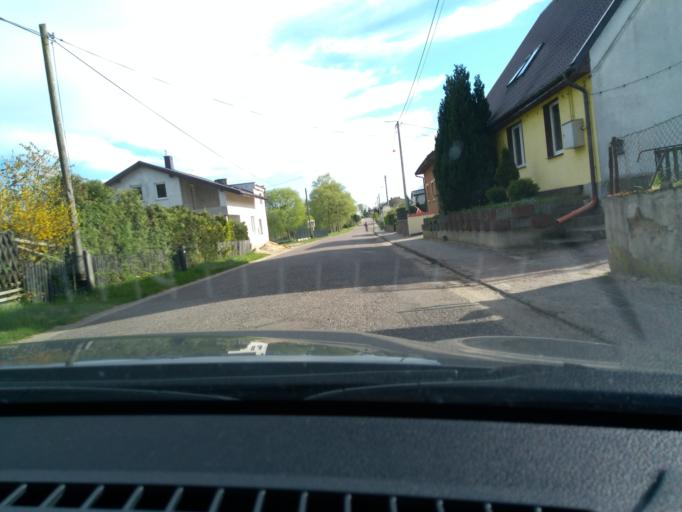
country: PL
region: Pomeranian Voivodeship
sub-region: Powiat leborski
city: Cewice
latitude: 54.3348
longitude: 17.6848
